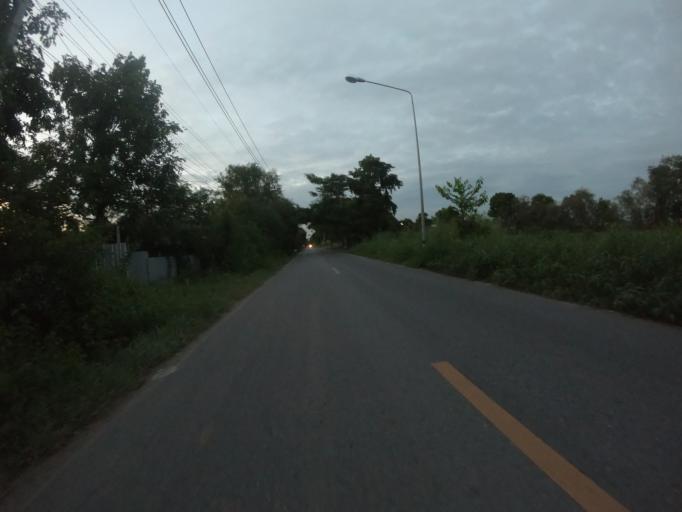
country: TH
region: Pathum Thani
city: Ban Rangsit
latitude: 14.0340
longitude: 100.8006
